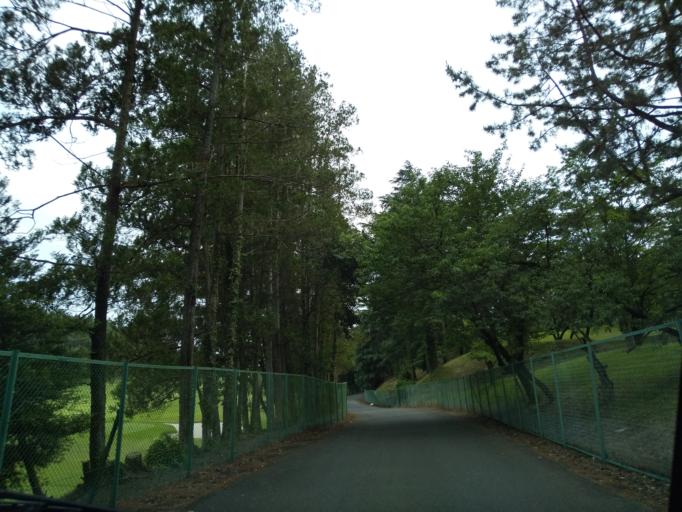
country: JP
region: Kanagawa
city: Atsugi
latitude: 35.4781
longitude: 139.3248
